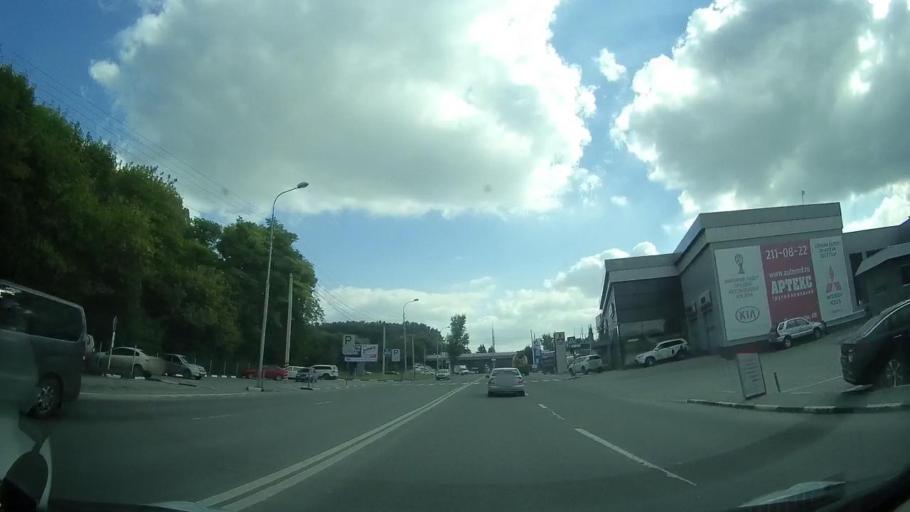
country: RU
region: Rostov
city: Imeni Chkalova
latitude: 47.2563
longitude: 39.7939
